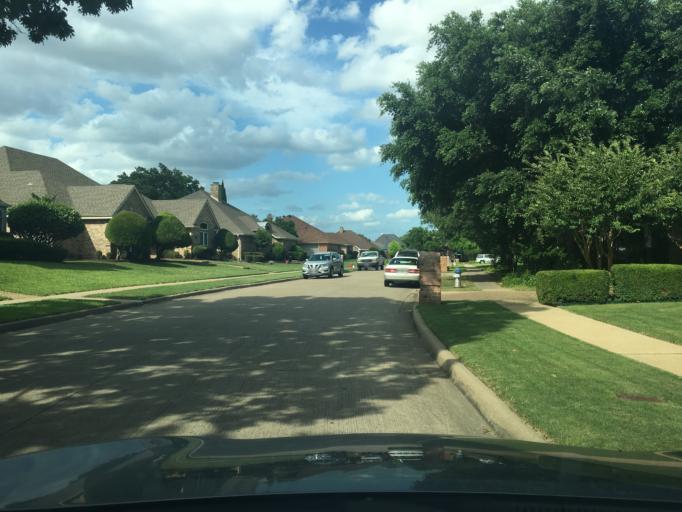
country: US
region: Texas
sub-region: Dallas County
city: Garland
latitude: 32.9324
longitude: -96.6715
